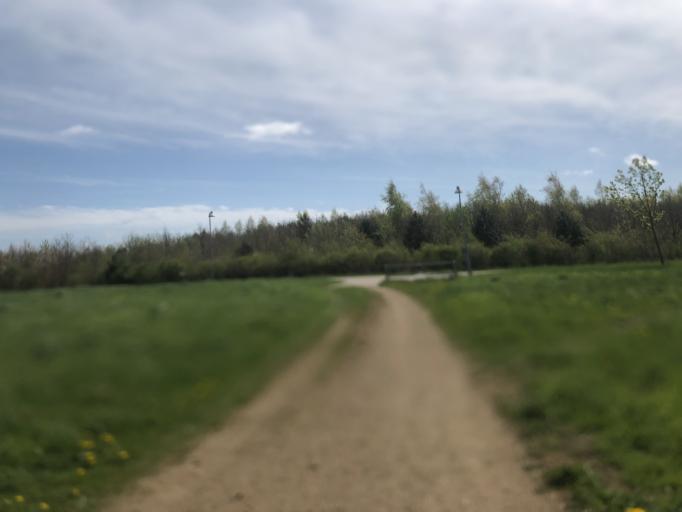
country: DK
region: Zealand
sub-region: Ringsted Kommune
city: Ringsted
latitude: 55.4529
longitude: 11.8218
